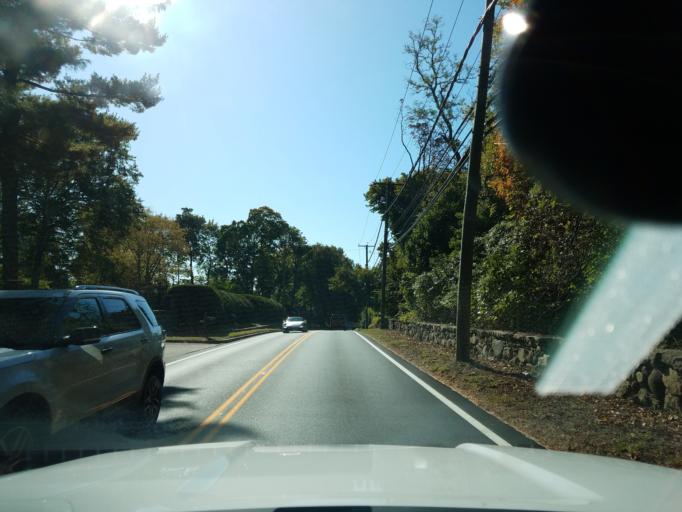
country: US
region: Connecticut
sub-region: Fairfield County
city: Cos Cob
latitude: 41.0617
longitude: -73.6186
